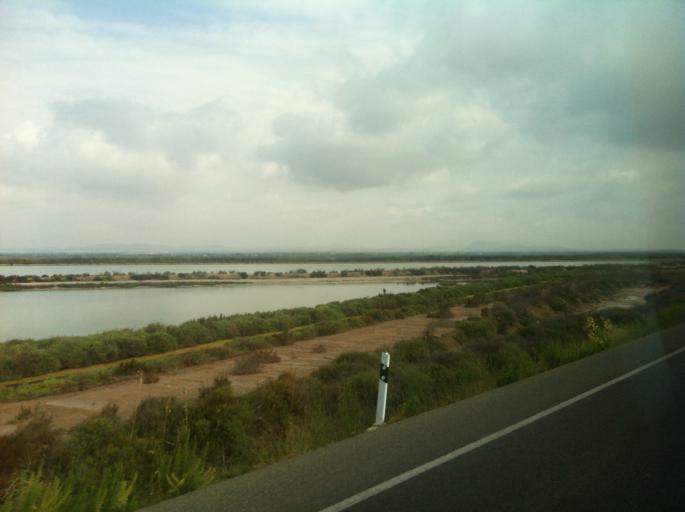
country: ES
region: Valencia
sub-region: Provincia de Alicante
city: Santa Pola
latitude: 38.1749
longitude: -0.6223
